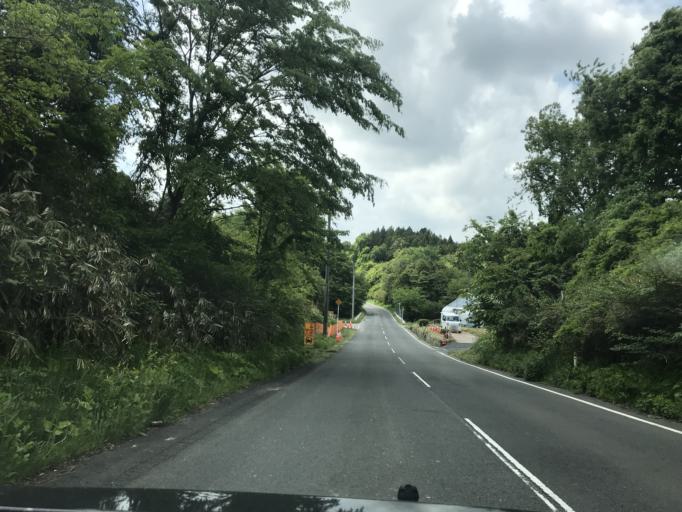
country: JP
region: Miyagi
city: Furukawa
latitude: 38.7614
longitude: 140.9397
